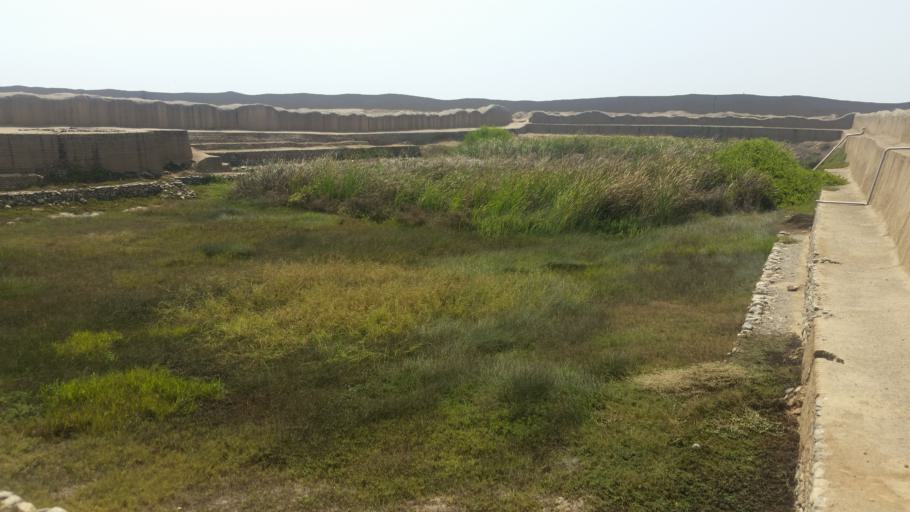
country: PE
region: La Libertad
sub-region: Provincia de Trujillo
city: Buenos Aires
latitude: -8.1111
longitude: -79.0743
